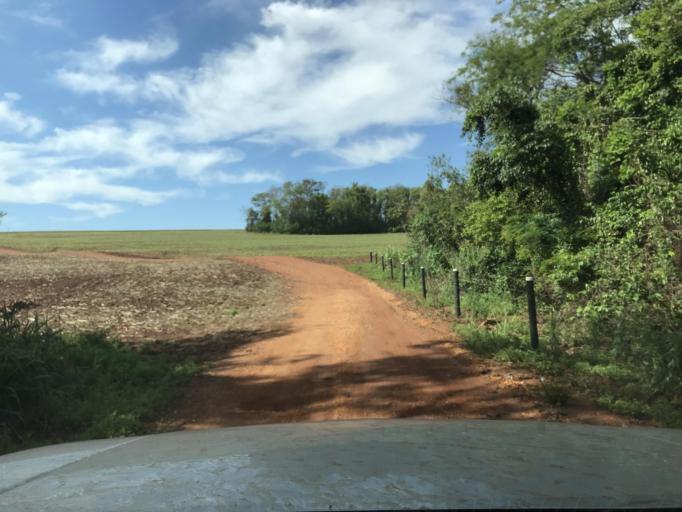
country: BR
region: Parana
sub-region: Palotina
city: Palotina
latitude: -24.1815
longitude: -53.8395
